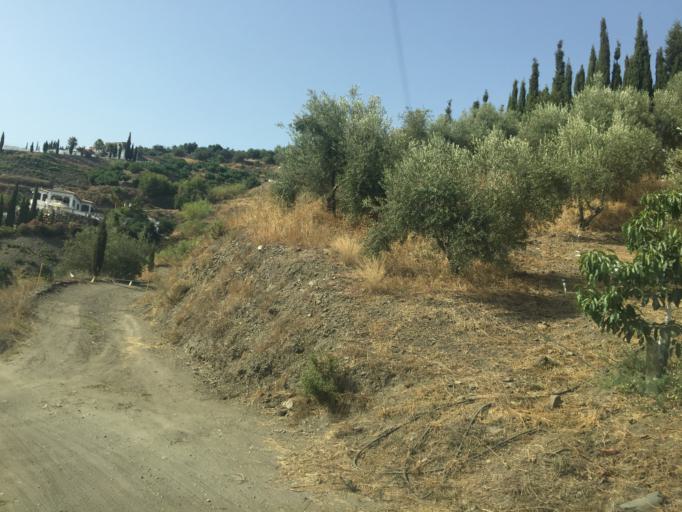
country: ES
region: Andalusia
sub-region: Provincia de Malaga
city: Frigiliana
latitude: 36.8064
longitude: -3.9260
